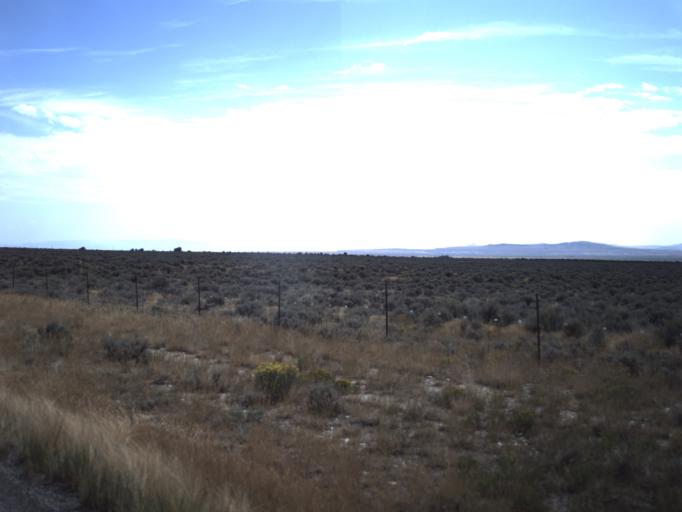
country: US
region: Idaho
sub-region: Cassia County
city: Burley
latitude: 41.8164
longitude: -113.3765
